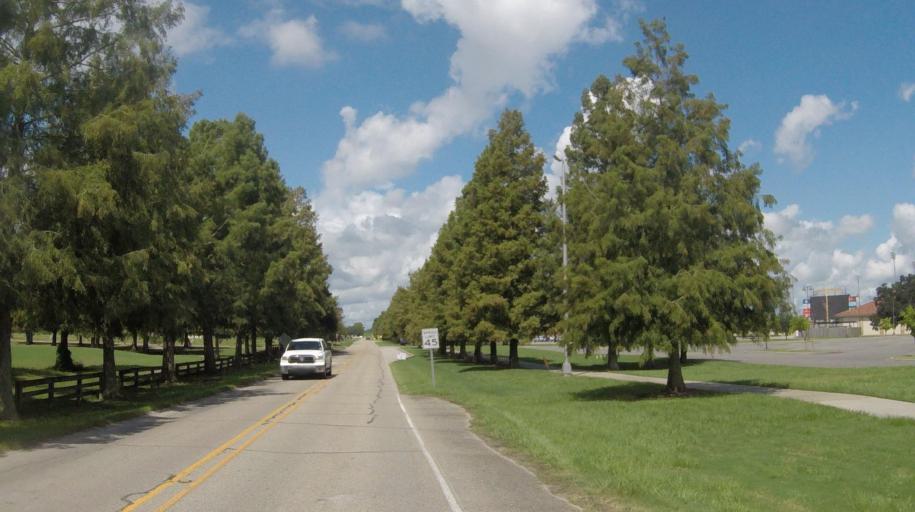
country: US
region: Louisiana
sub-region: West Baton Rouge Parish
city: Port Allen
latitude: 30.4047
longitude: -91.1846
